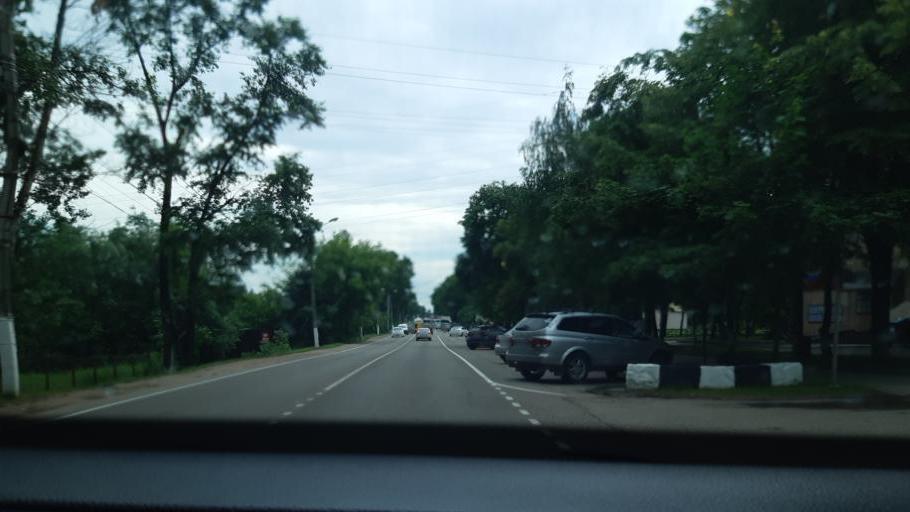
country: RU
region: Moskovskaya
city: Bol'shiye Vyazemy
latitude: 55.6235
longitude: 36.9837
